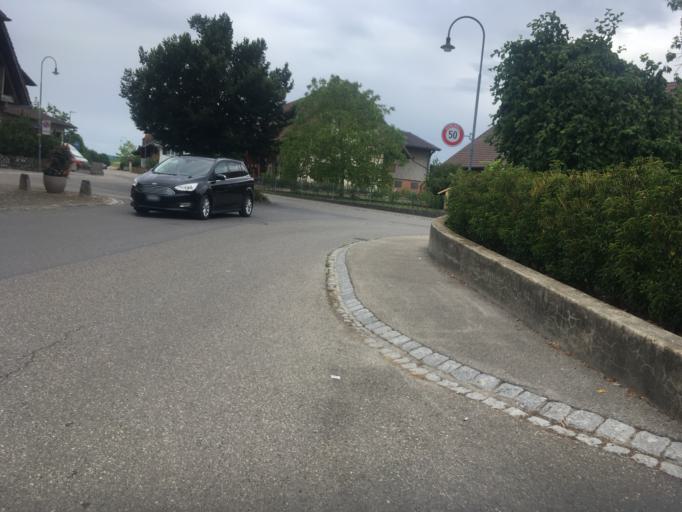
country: CH
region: Bern
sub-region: Seeland District
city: Erlach
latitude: 47.0325
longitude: 7.1109
